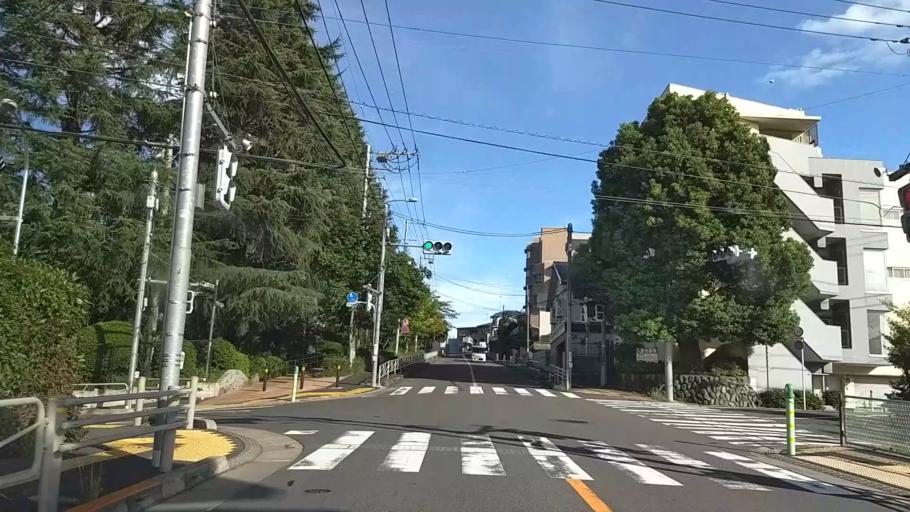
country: JP
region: Tokyo
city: Hachioji
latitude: 35.6513
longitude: 139.3199
